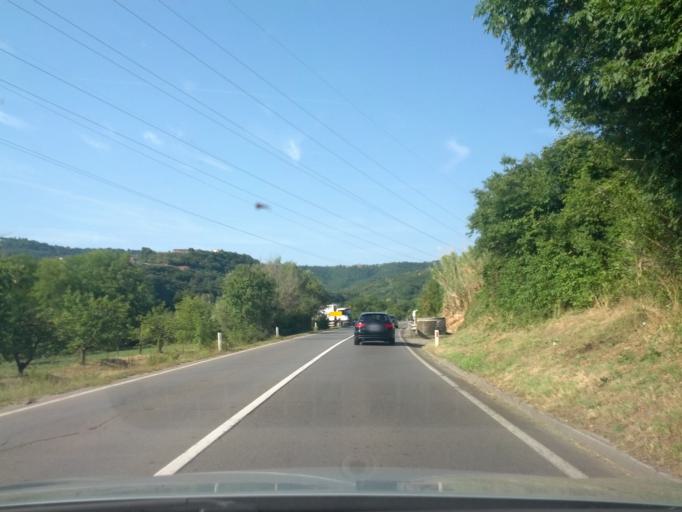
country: SI
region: Koper-Capodistria
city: Koper
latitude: 45.5252
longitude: 13.7334
